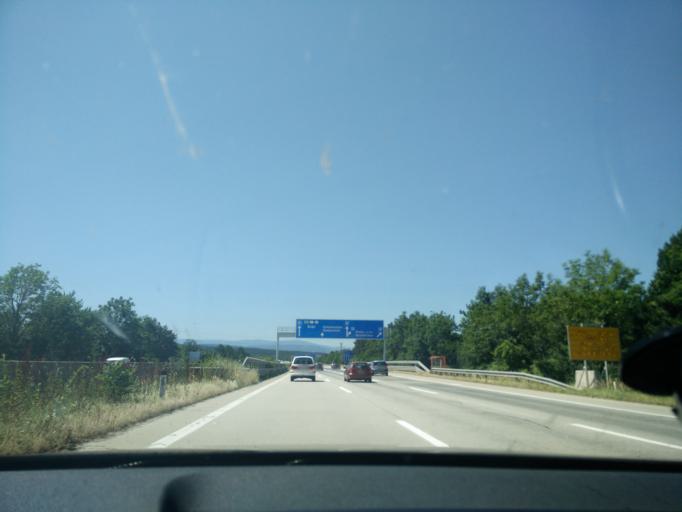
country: AT
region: Lower Austria
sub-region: Politischer Bezirk Neunkirchen
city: Breitenau
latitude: 47.7243
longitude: 16.1439
